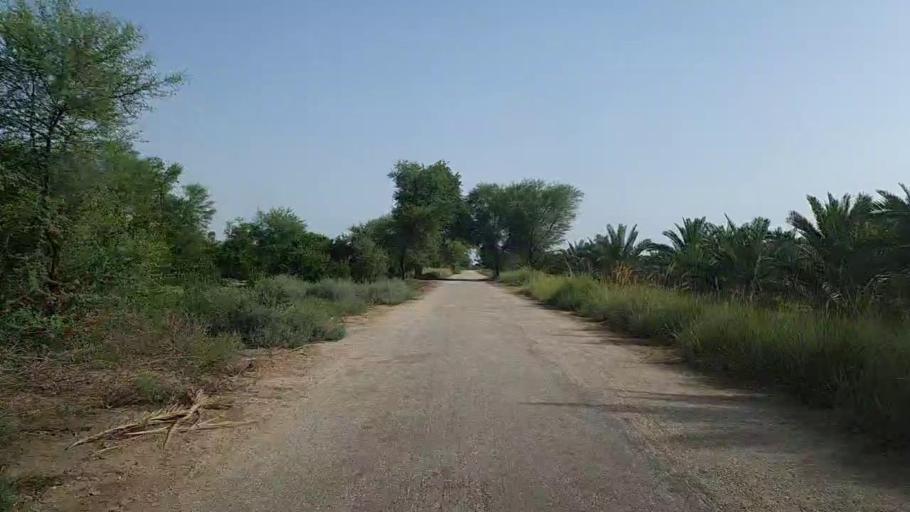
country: PK
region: Sindh
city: Karaundi
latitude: 26.8566
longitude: 68.3309
